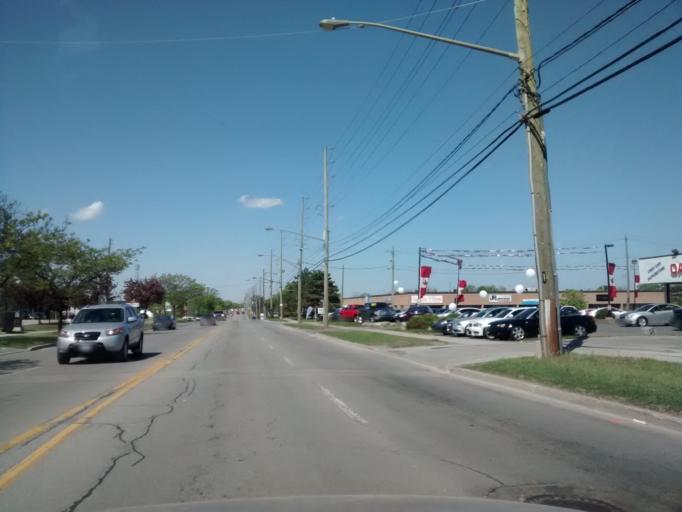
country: CA
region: Ontario
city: Oakville
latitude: 43.4205
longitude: -79.7157
